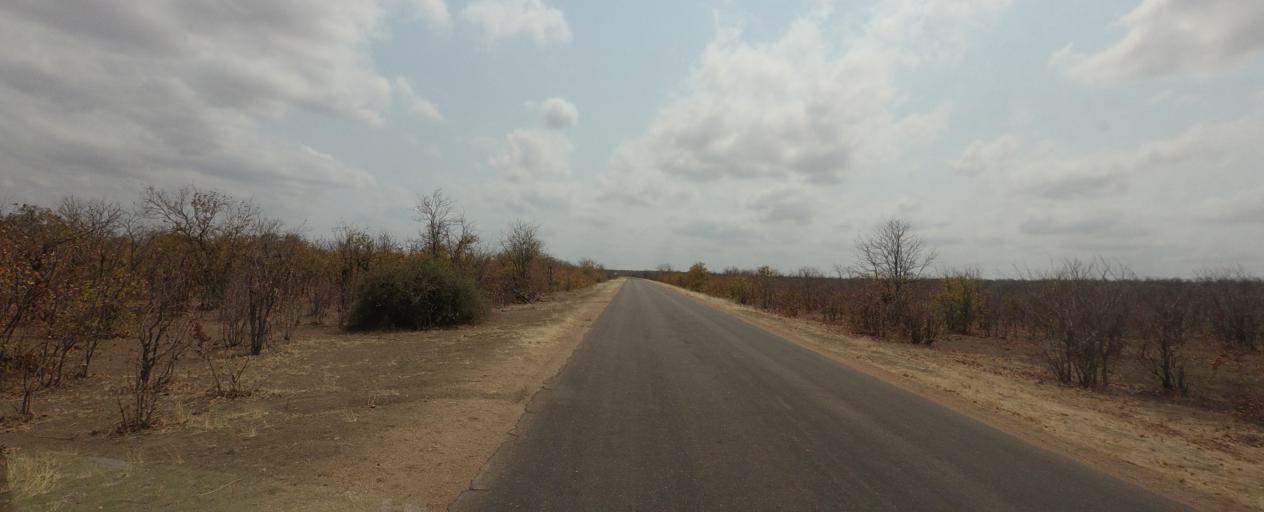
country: ZA
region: Limpopo
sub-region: Mopani District Municipality
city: Phalaborwa
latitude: -23.6030
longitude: 31.4547
